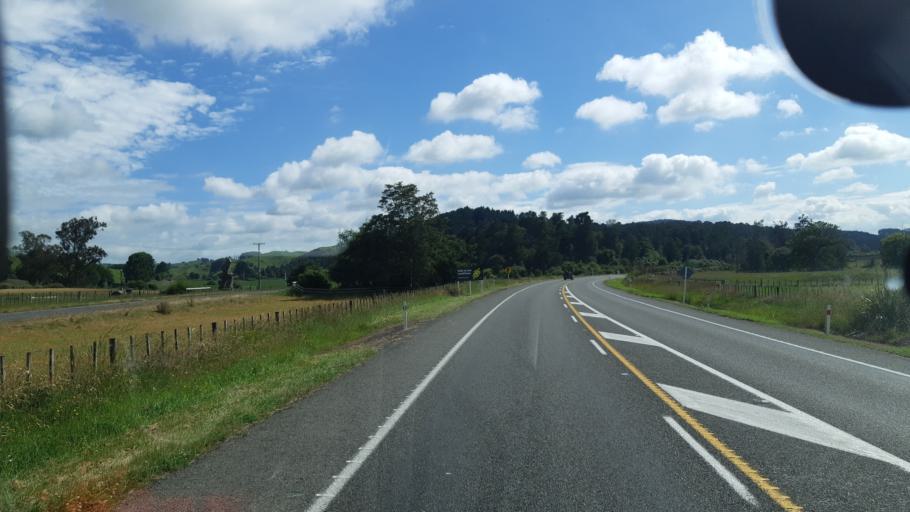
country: NZ
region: Manawatu-Wanganui
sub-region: Rangitikei District
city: Bulls
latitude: -39.9671
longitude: 175.5226
